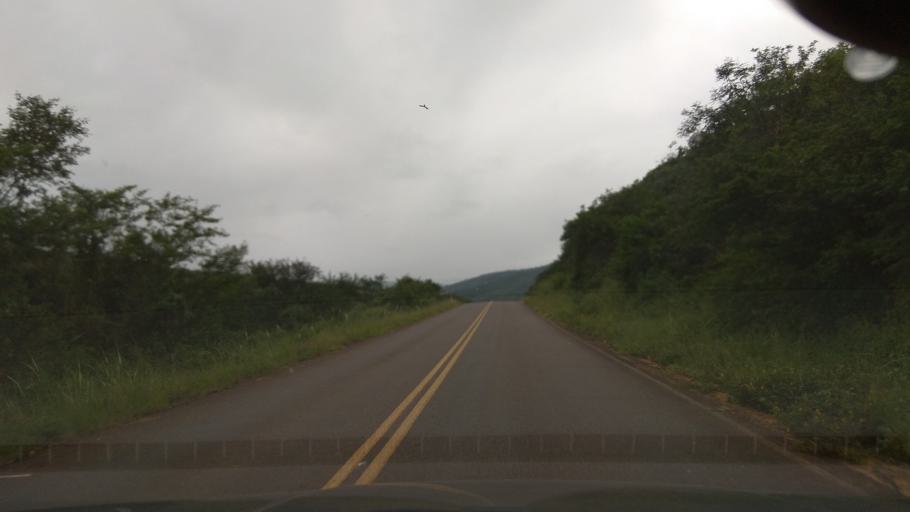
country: BR
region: Bahia
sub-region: Santa Ines
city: Santa Ines
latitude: -13.2523
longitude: -39.7797
